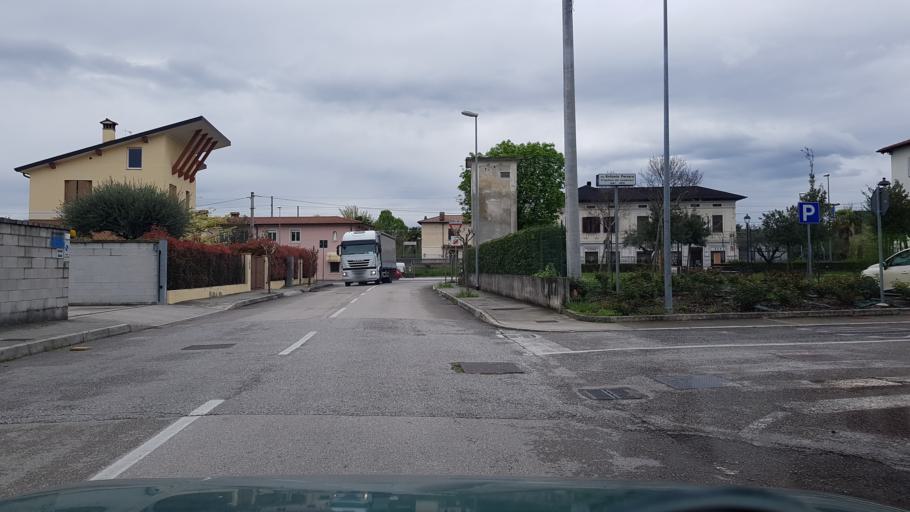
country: IT
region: Friuli Venezia Giulia
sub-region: Provincia di Gorizia
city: Mossa
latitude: 45.9342
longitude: 13.5474
